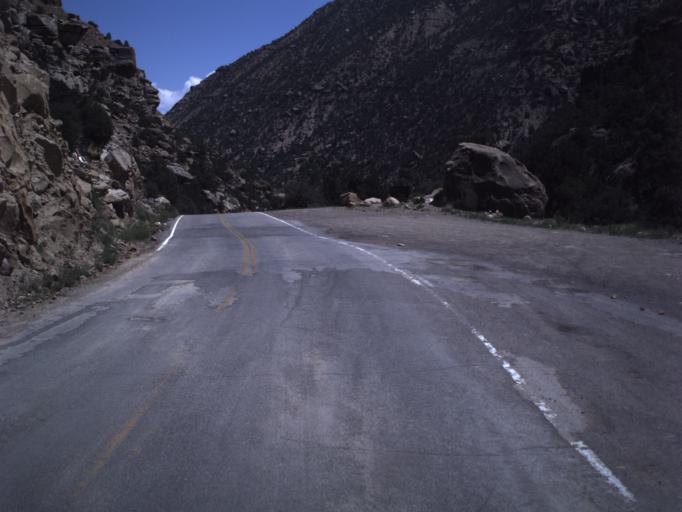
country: US
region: Utah
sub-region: Emery County
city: Orangeville
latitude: 39.2748
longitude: -111.2066
